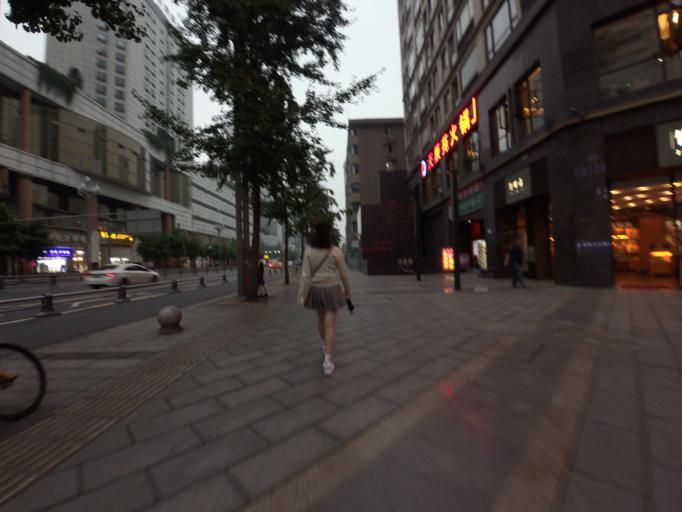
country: CN
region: Sichuan
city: Chengdu
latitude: 30.6729
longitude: 104.0642
